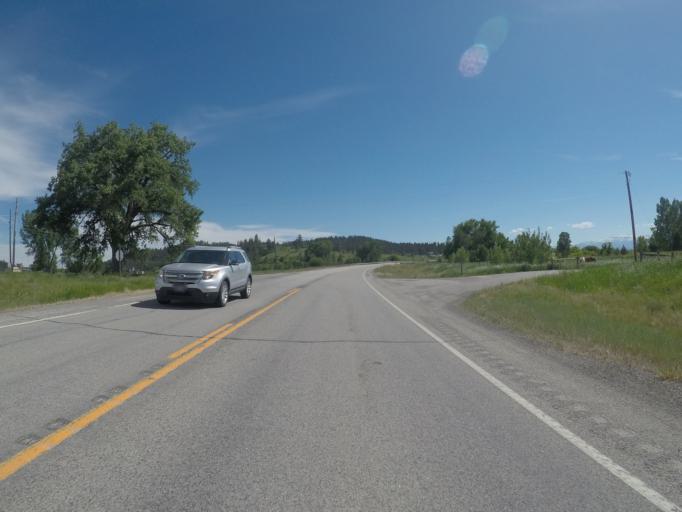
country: US
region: Montana
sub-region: Stillwater County
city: Columbus
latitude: 45.6146
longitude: -109.2795
